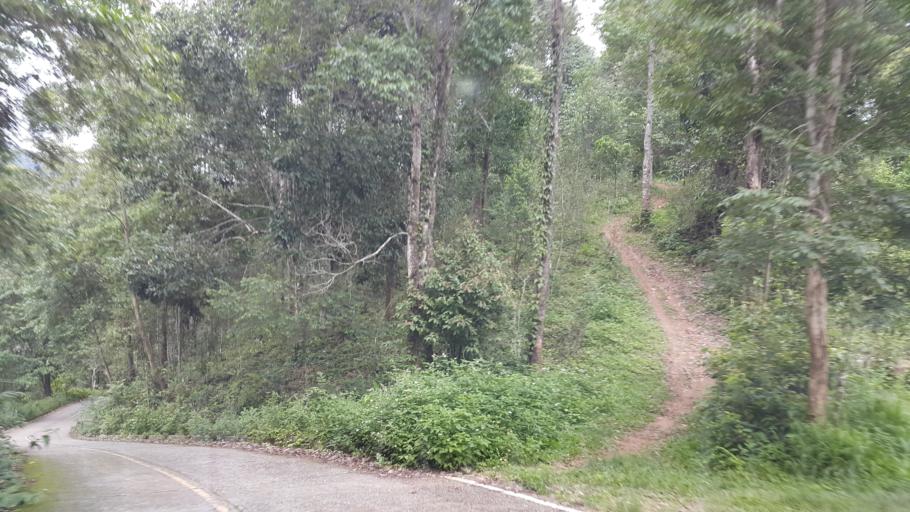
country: TH
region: Lampang
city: Mueang Pan
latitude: 18.8313
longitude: 99.3802
